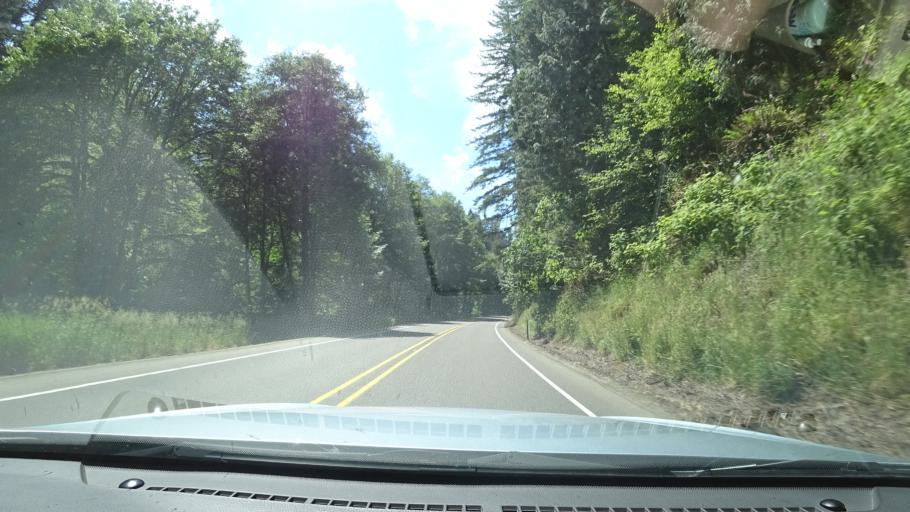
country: US
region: Oregon
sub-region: Lane County
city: Florence
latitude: 44.0070
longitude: -123.7322
